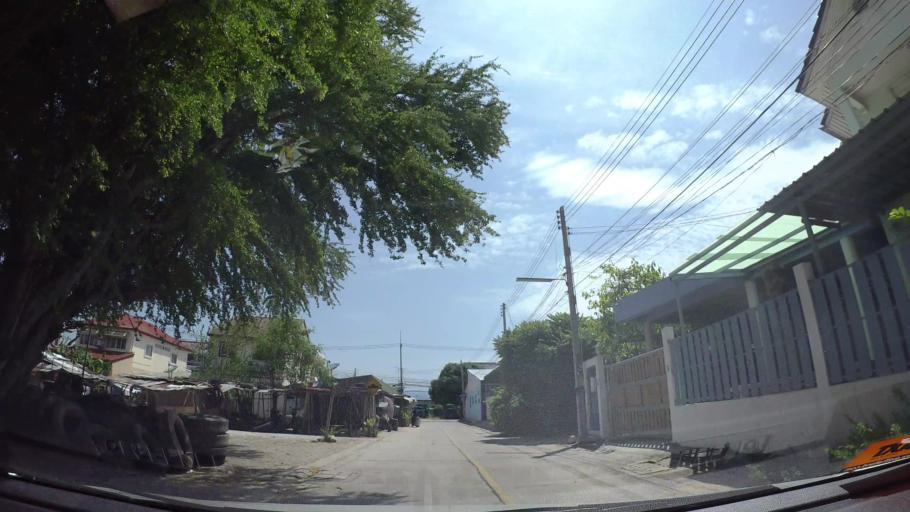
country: TH
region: Chon Buri
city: Chon Buri
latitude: 13.3174
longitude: 100.9571
